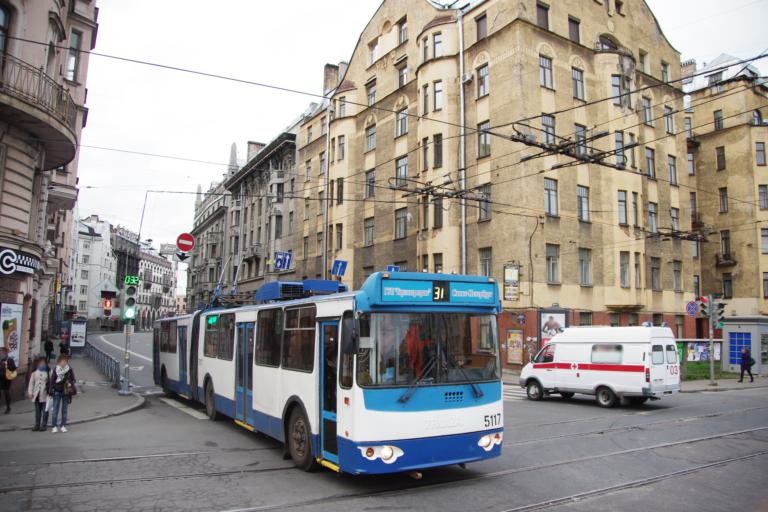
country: RU
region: St.-Petersburg
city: Petrogradka
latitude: 59.9679
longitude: 30.3143
